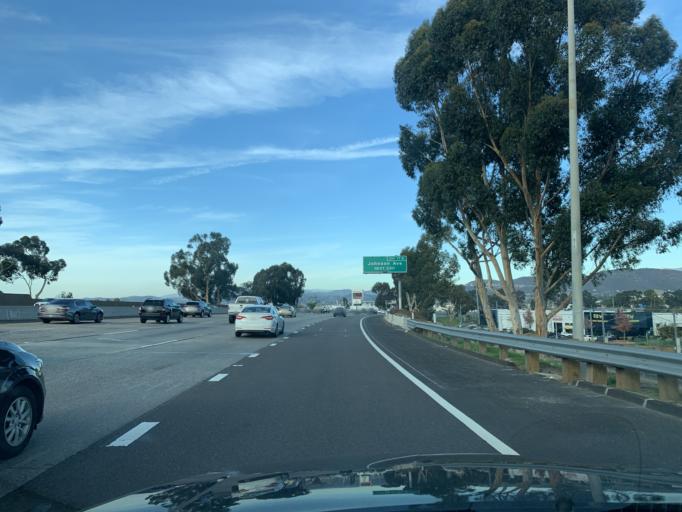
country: US
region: California
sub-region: San Diego County
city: El Cajon
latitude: 32.7978
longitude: -116.9765
